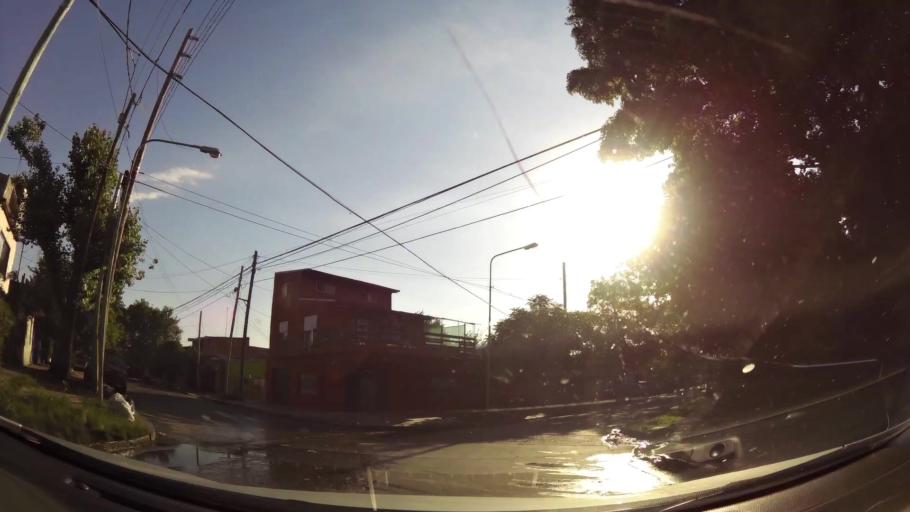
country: AR
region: Buenos Aires
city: Santa Catalina - Dique Lujan
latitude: -34.4616
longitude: -58.6645
